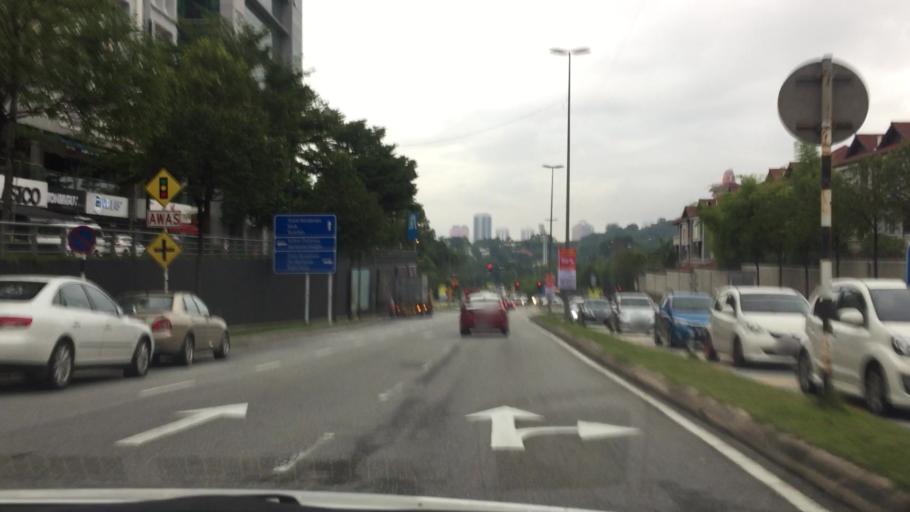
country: MY
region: Kuala Lumpur
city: Kuala Lumpur
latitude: 3.1704
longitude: 101.6653
